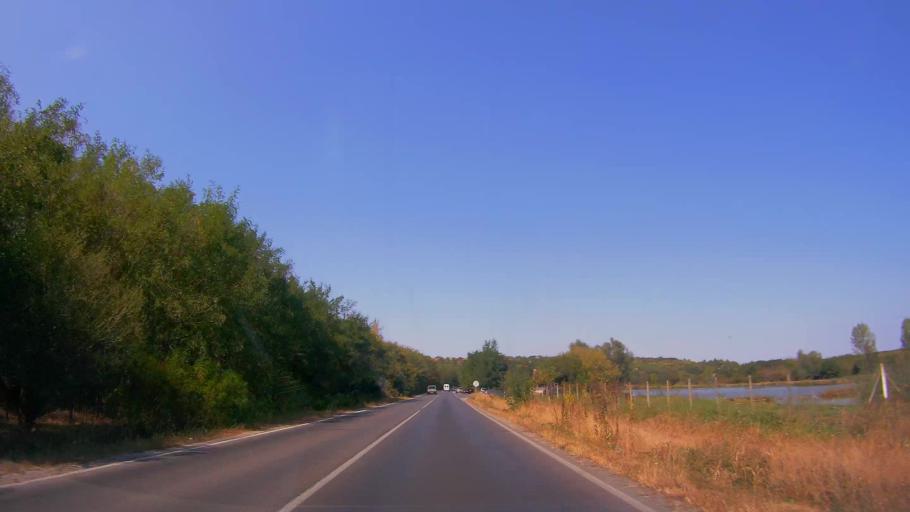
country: BG
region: Razgrad
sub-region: Obshtina Tsar Kaloyan
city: Tsar Kaloyan
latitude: 43.6166
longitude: 26.2140
